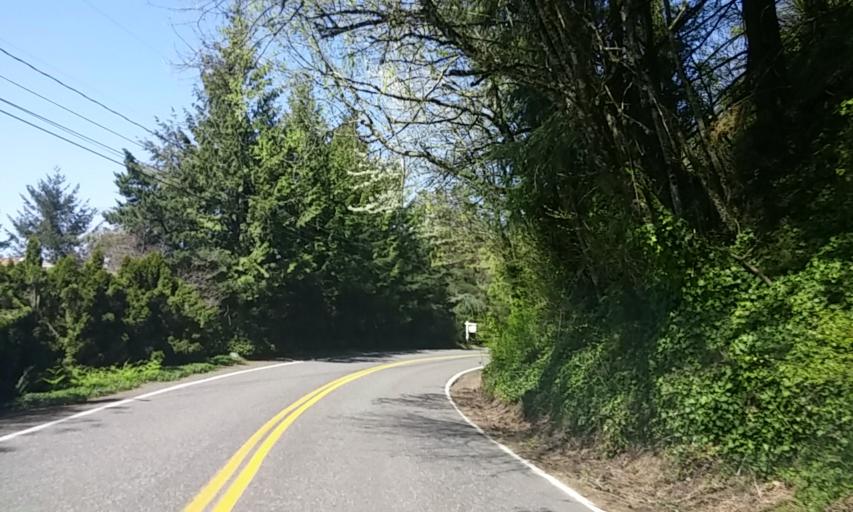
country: US
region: Oregon
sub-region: Washington County
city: West Haven-Sylvan
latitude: 45.5272
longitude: -122.7569
